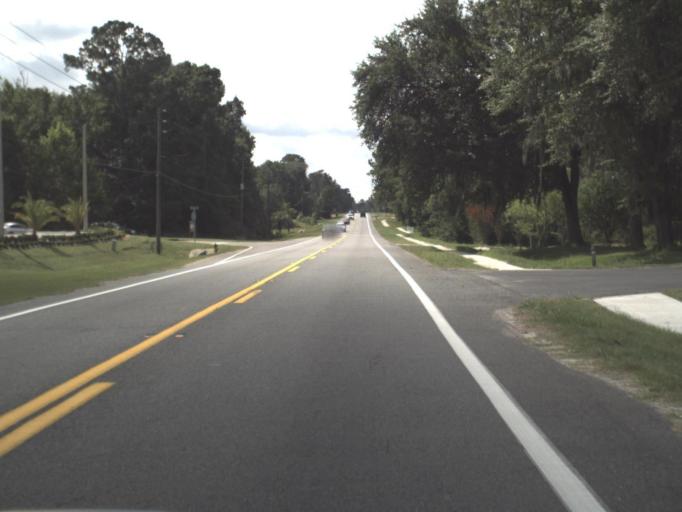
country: US
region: Florida
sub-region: Baker County
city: Macclenny
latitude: 30.2722
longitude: -82.1190
